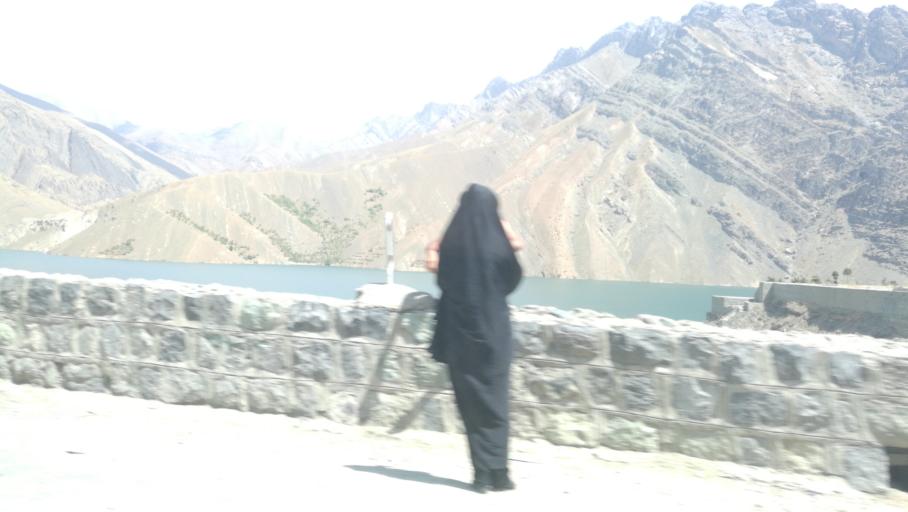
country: IR
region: Alborz
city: Karaj
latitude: 35.9677
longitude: 51.0936
